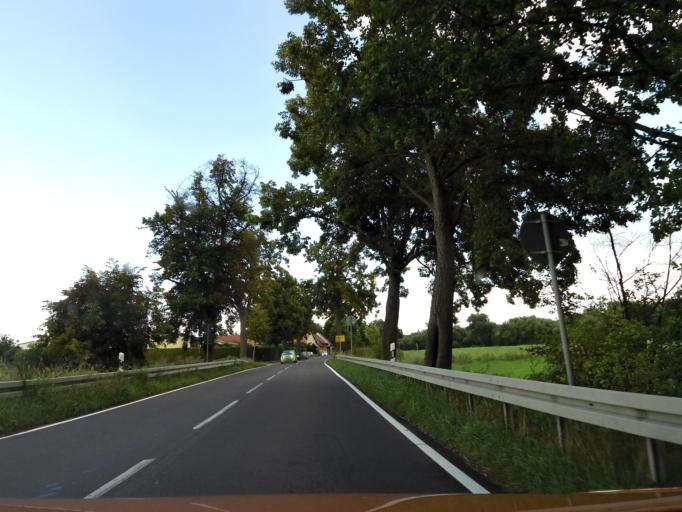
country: DE
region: Brandenburg
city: Potsdam
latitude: 52.4630
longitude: 13.0085
